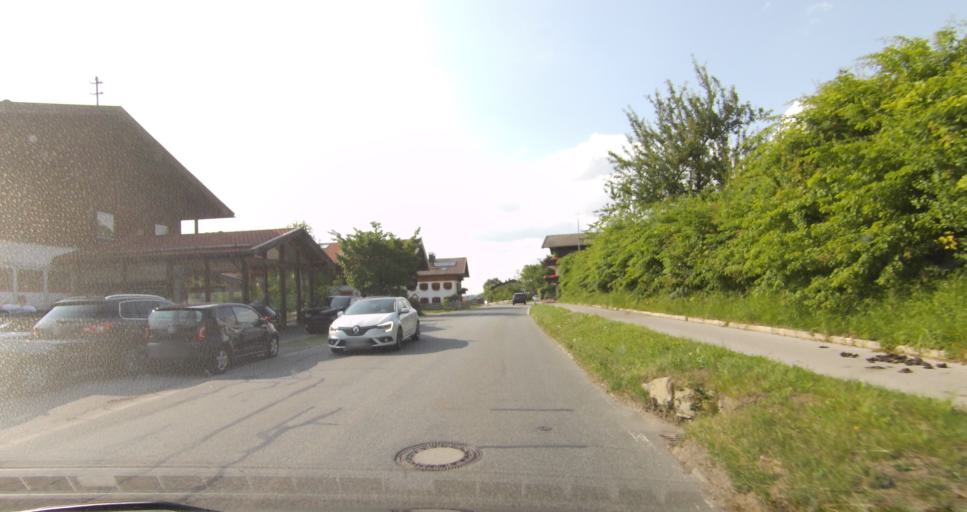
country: DE
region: Bavaria
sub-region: Upper Bavaria
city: Fischbachau
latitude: 47.7450
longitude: 11.9503
